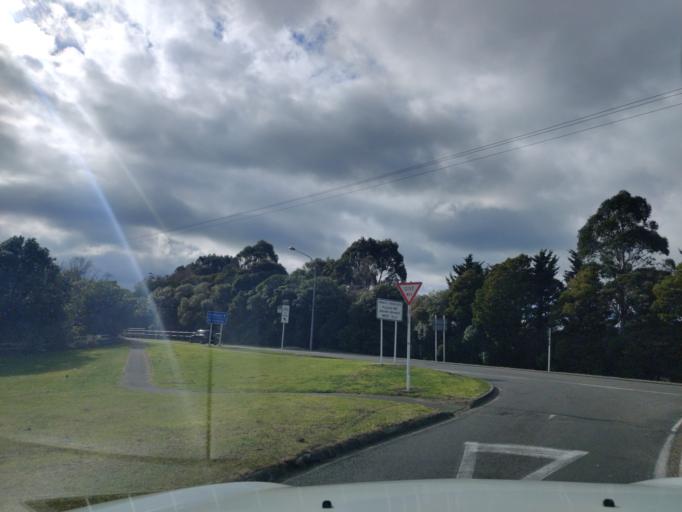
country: NZ
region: Manawatu-Wanganui
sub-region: Palmerston North City
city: Palmerston North
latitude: -40.2969
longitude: 175.7524
